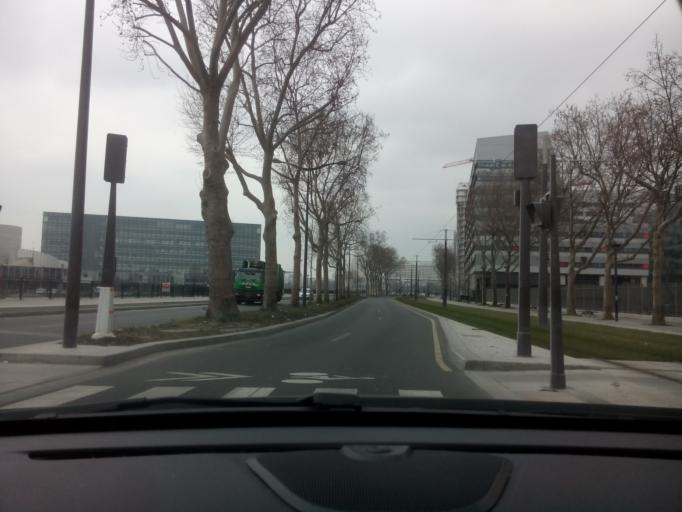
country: FR
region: Ile-de-France
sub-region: Departement du Val-de-Marne
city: Ivry-sur-Seine
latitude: 48.8273
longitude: 2.3850
